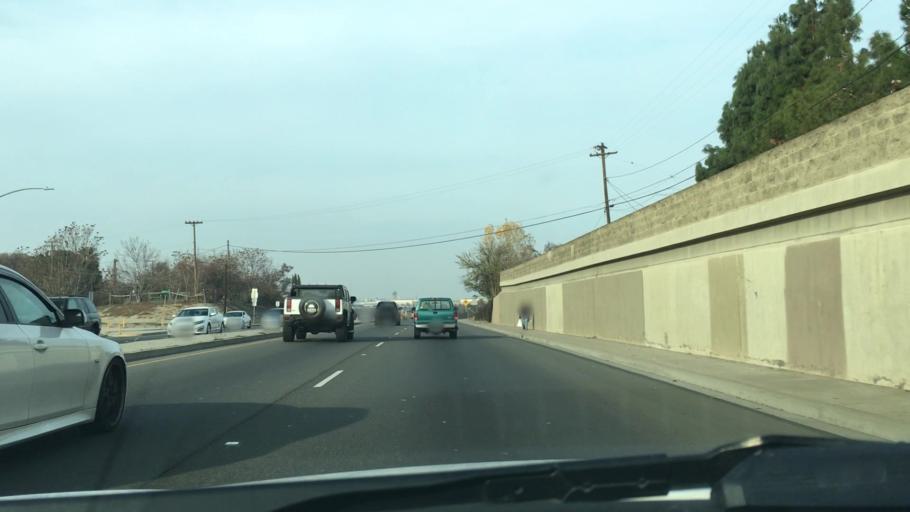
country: US
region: California
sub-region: Stanislaus County
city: Ceres
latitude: 37.6138
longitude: -120.9386
